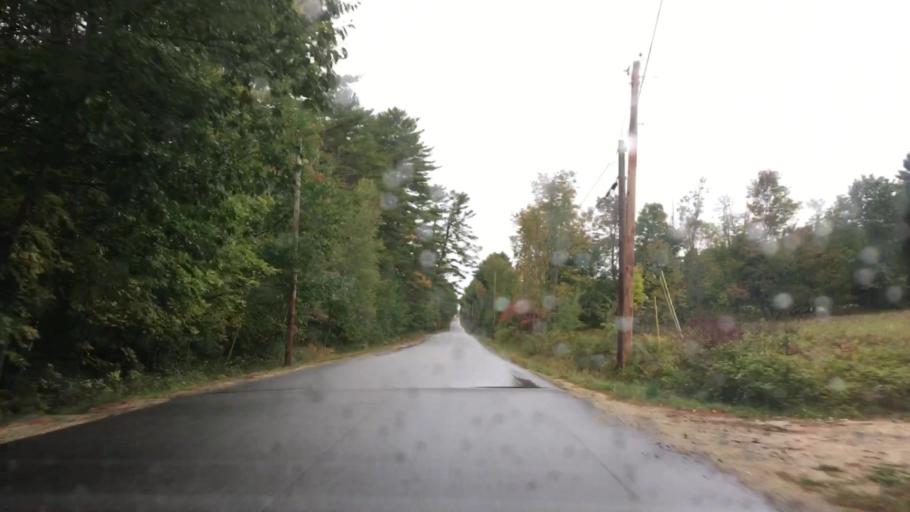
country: US
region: Maine
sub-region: Cumberland County
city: Harrison
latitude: 44.0874
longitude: -70.6503
